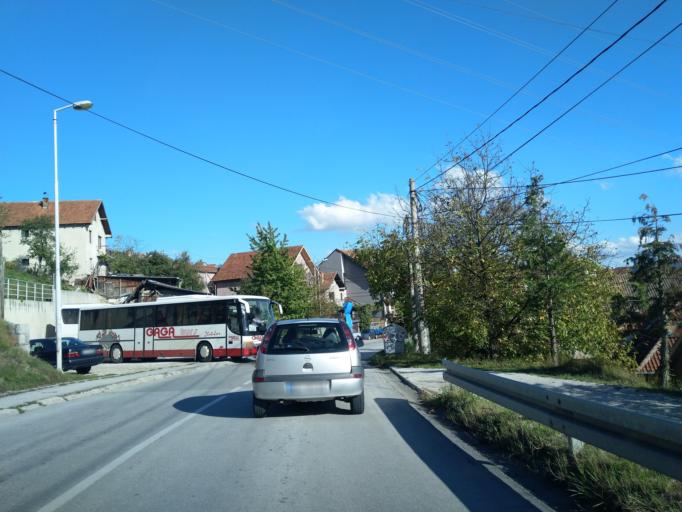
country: RS
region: Central Serbia
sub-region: Zlatiborski Okrug
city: Uzice
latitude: 43.8615
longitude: 19.8221
